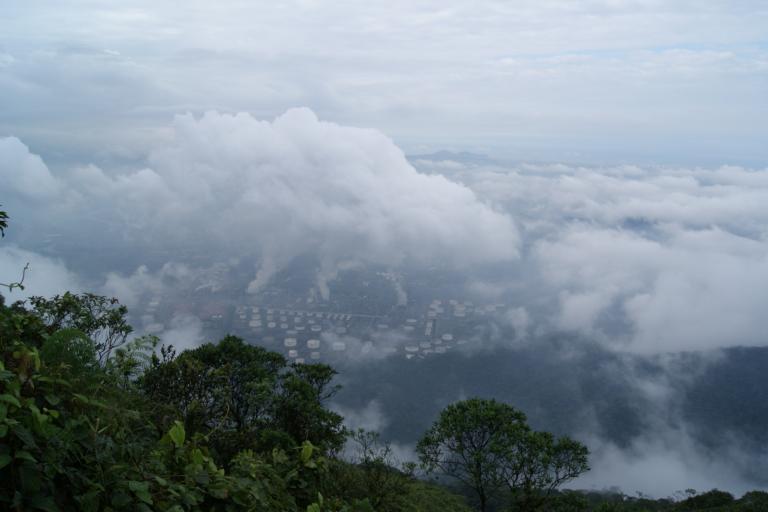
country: BR
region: Sao Paulo
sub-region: Cubatao
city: Cubatao
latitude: -23.8507
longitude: -46.4463
